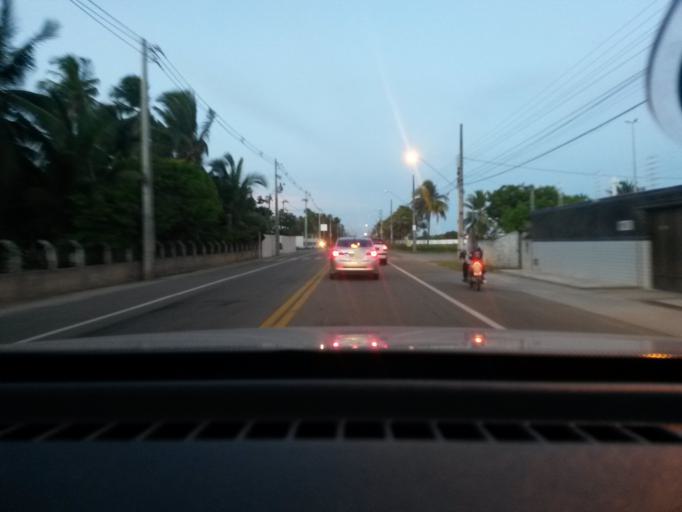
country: BR
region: Sergipe
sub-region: Sao Cristovao
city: Sao Cristovao
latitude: -11.0643
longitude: -37.1168
